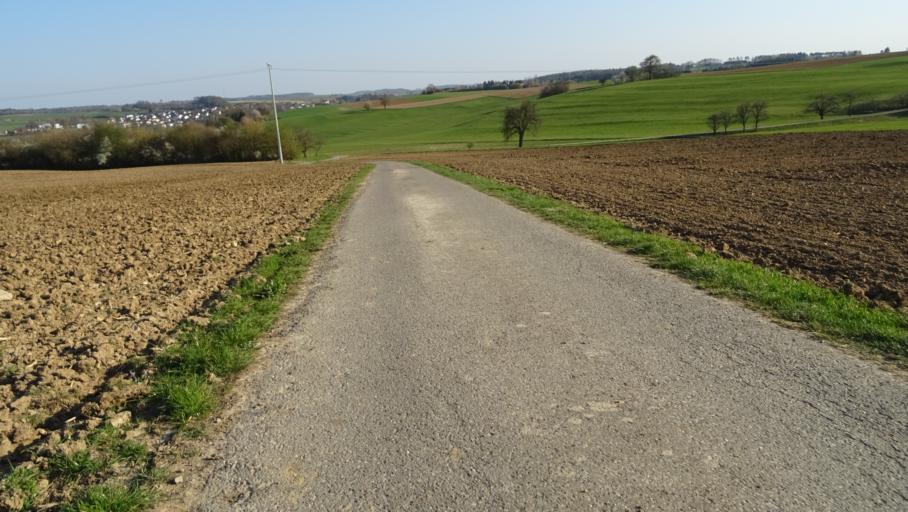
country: DE
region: Baden-Wuerttemberg
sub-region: Karlsruhe Region
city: Billigheim
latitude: 49.4073
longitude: 9.2594
